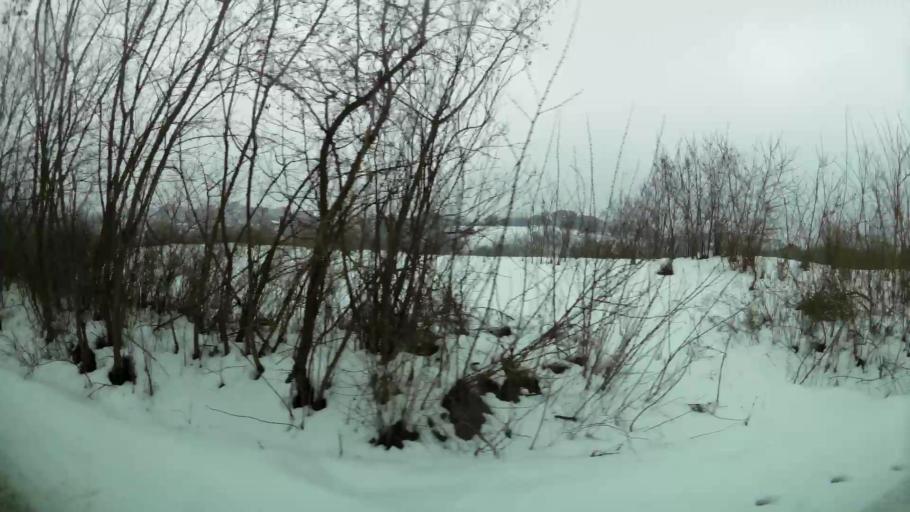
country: RS
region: Central Serbia
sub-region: Belgrade
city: Zvezdara
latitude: 44.7490
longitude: 20.5226
